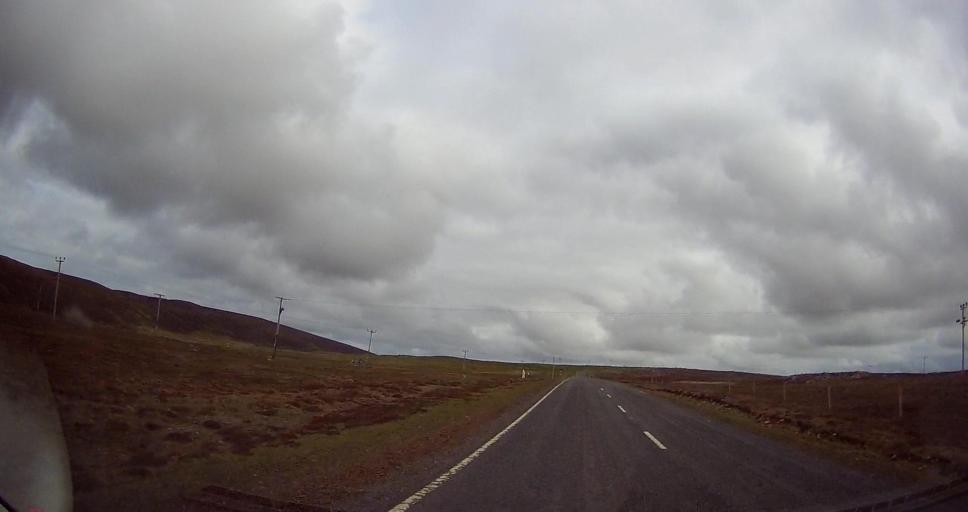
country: GB
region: Scotland
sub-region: Shetland Islands
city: Shetland
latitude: 60.7189
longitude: -0.9119
